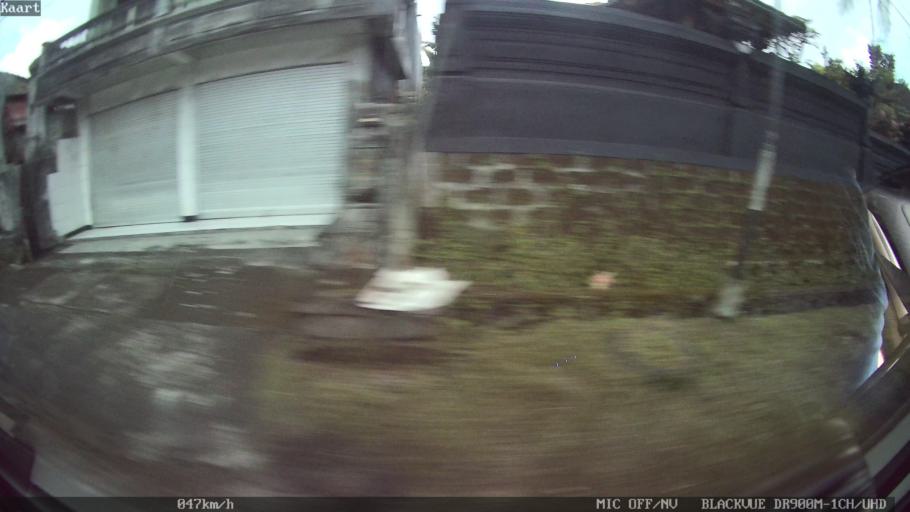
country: ID
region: Bali
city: Penebel
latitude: -8.4190
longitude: 115.1458
